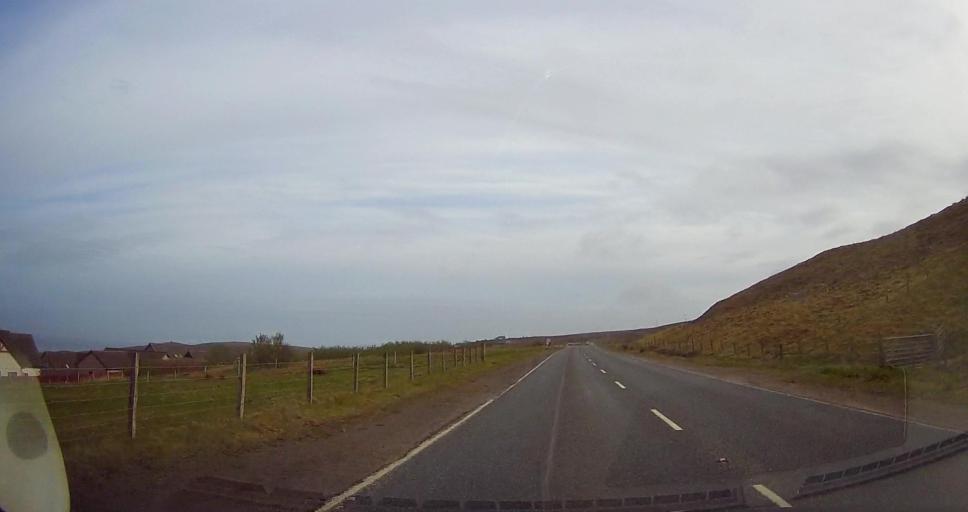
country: GB
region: Scotland
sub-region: Shetland Islands
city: Lerwick
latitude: 60.1300
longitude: -1.2152
